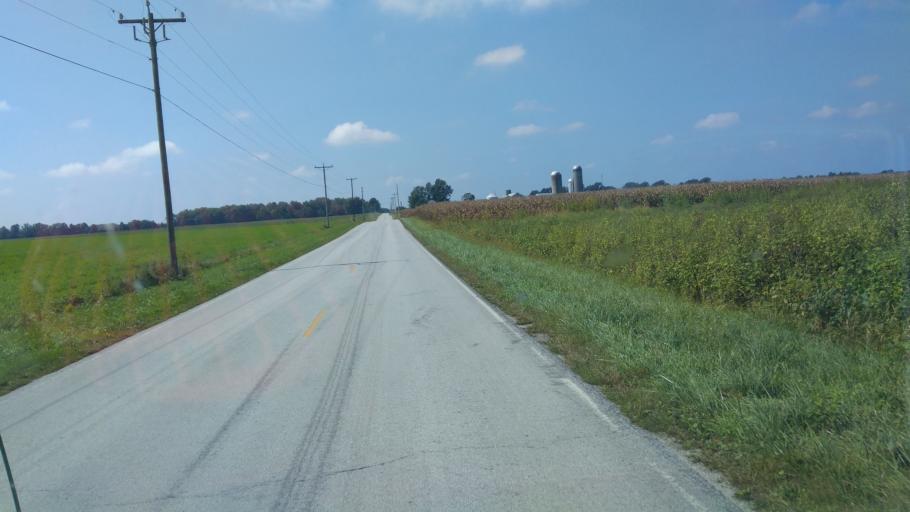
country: US
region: Ohio
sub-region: Hardin County
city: Kenton
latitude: 40.6664
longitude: -83.5800
